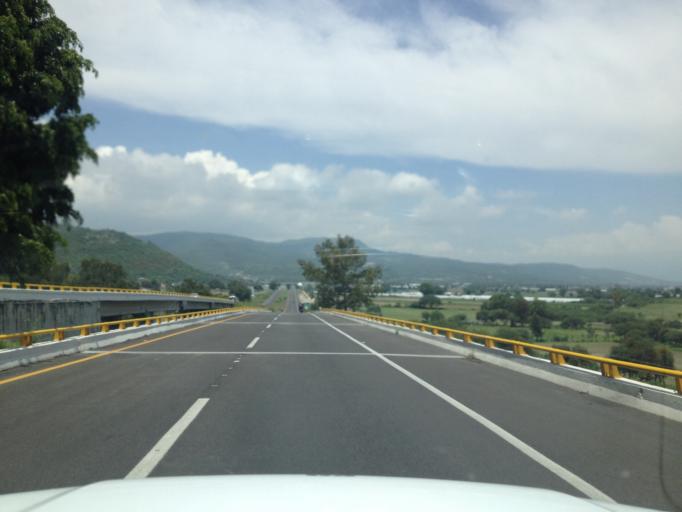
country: MX
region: Michoacan
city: Copandaro de Galeana
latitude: 19.8874
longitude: -101.1840
